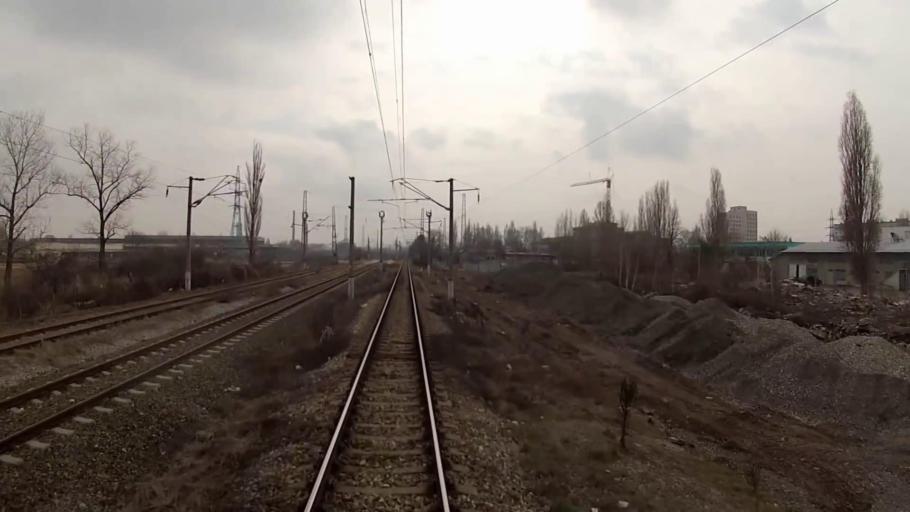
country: BG
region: Sofia-Capital
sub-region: Stolichna Obshtina
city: Sofia
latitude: 42.6631
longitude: 23.4198
